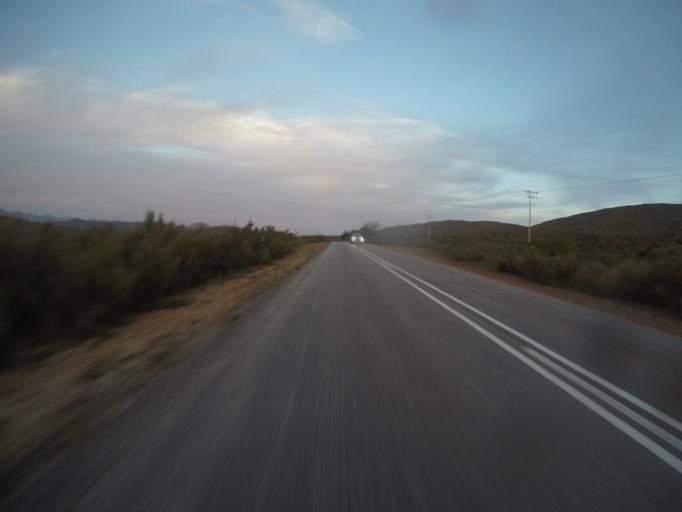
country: ZA
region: Western Cape
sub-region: Eden District Municipality
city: Plettenberg Bay
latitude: -33.7419
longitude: 23.4416
